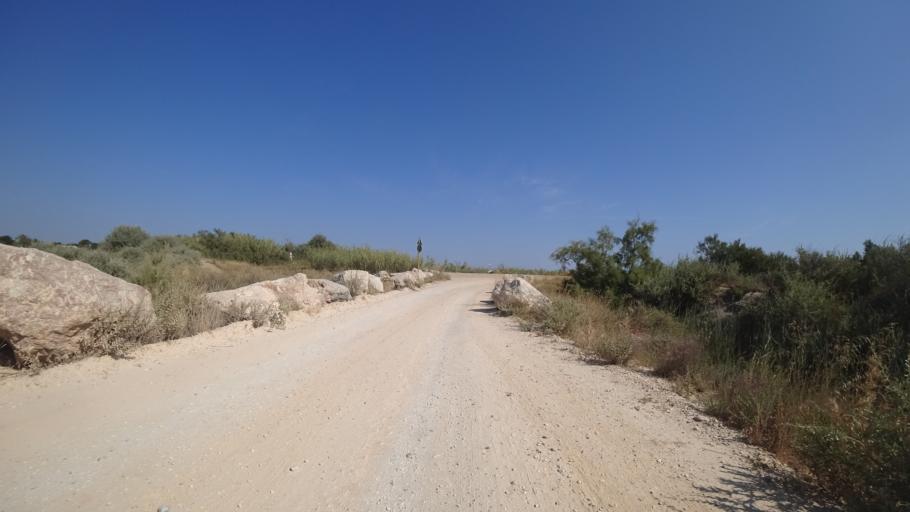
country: FR
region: Languedoc-Roussillon
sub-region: Departement des Pyrenees-Orientales
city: Le Barcares
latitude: 42.7777
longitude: 3.0371
